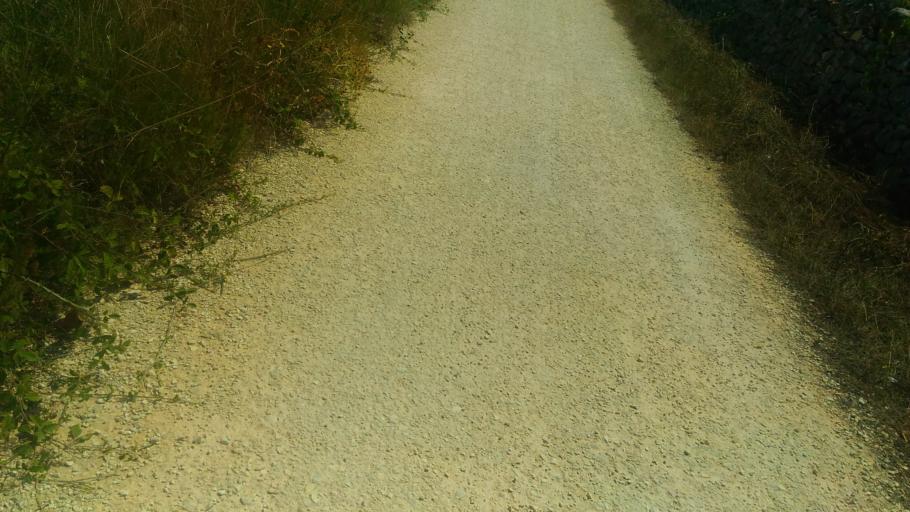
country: IT
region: Apulia
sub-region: Provincia di Brindisi
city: Cisternino
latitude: 40.7263
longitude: 17.3946
